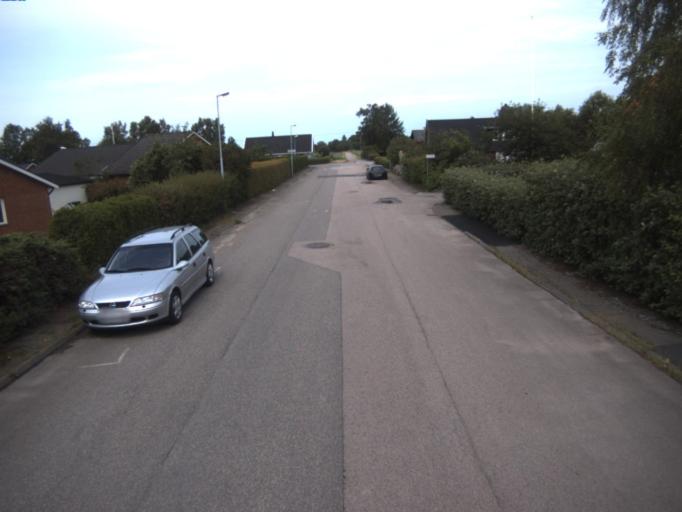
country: SE
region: Skane
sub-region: Helsingborg
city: Odakra
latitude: 56.1097
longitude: 12.7489
